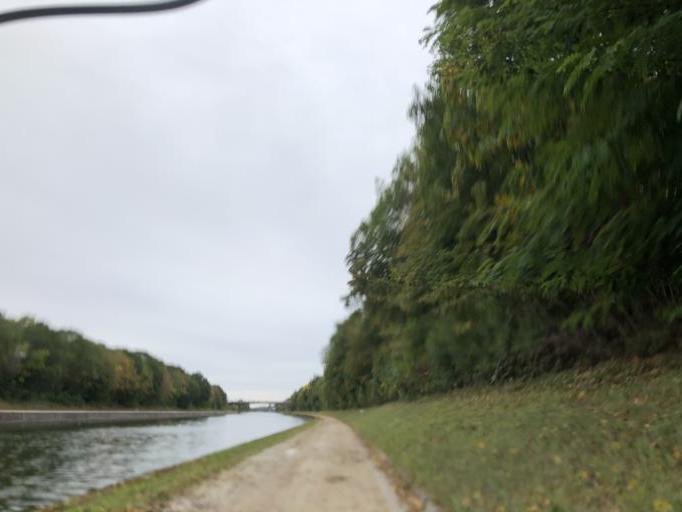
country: DE
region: Bavaria
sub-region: Regierungsbezirk Mittelfranken
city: Zirndorf
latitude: 49.4711
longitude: 10.9481
